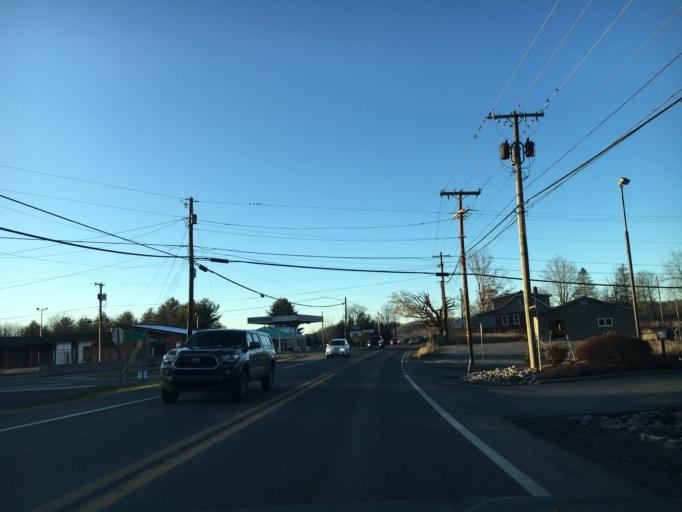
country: US
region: West Virginia
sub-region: Raleigh County
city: Daniels
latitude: 37.7432
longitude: -81.1227
